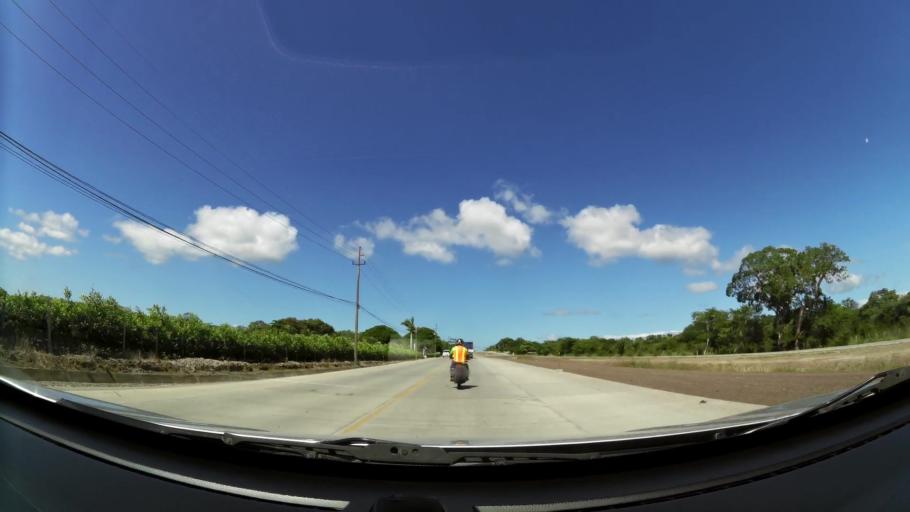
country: CR
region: Guanacaste
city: Bagaces
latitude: 10.5046
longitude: -85.2323
